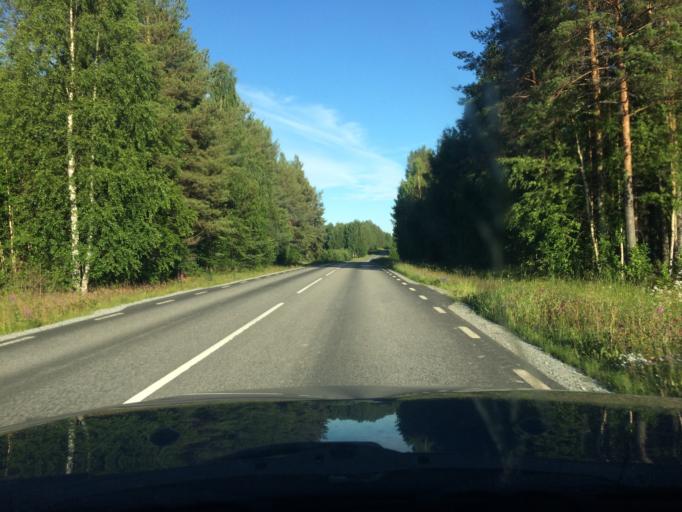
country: SE
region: Norrbotten
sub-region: Pitea Kommun
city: Roknas
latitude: 65.3369
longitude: 21.1897
